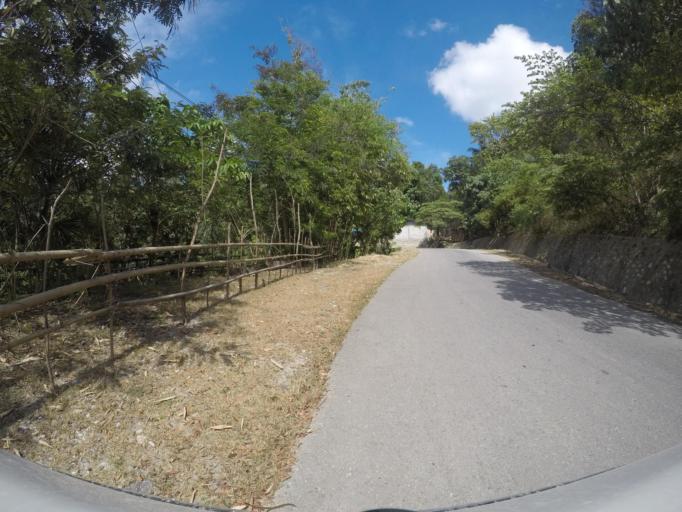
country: TL
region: Viqueque
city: Viqueque
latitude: -8.8690
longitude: 126.3625
